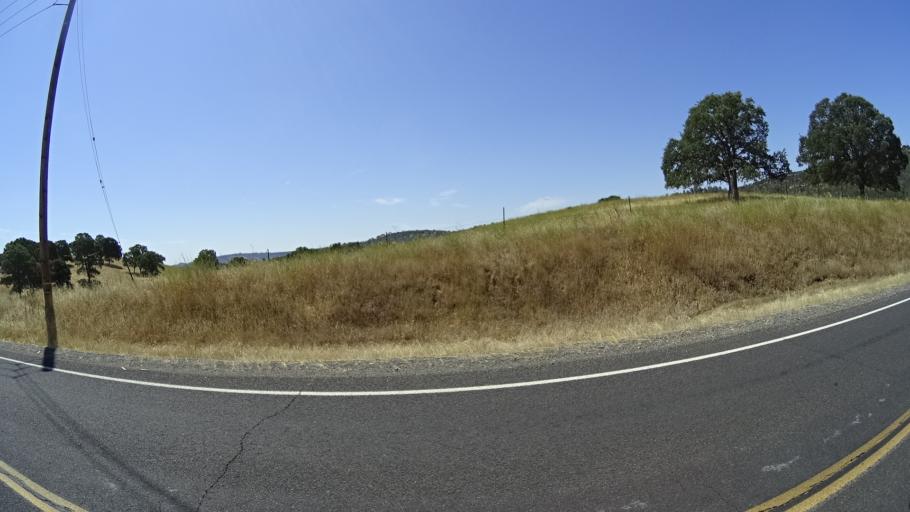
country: US
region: California
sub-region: Calaveras County
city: Copperopolis
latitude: 37.9362
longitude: -120.6175
